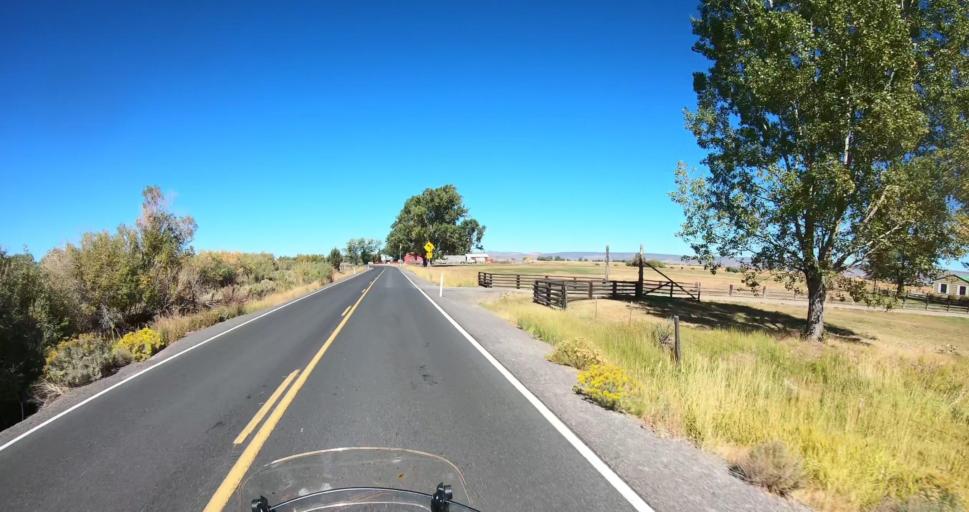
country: US
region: Oregon
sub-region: Lake County
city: Lakeview
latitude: 42.6827
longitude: -120.5283
